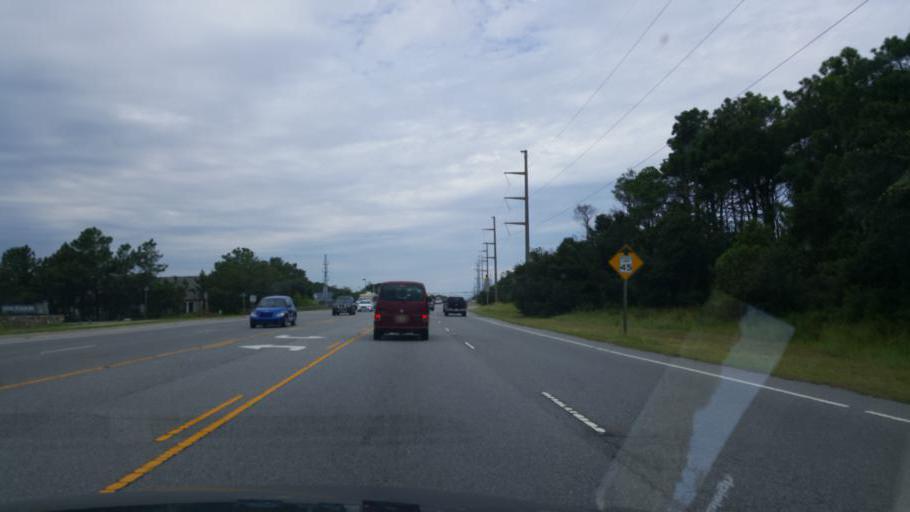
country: US
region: North Carolina
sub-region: Dare County
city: Nags Head
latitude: 35.9739
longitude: -75.6389
